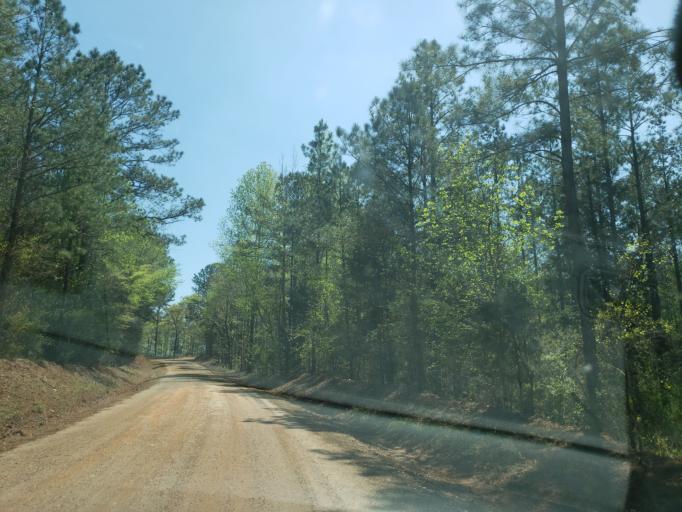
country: US
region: Alabama
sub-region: Tallapoosa County
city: Camp Hill
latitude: 32.6498
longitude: -85.6540
